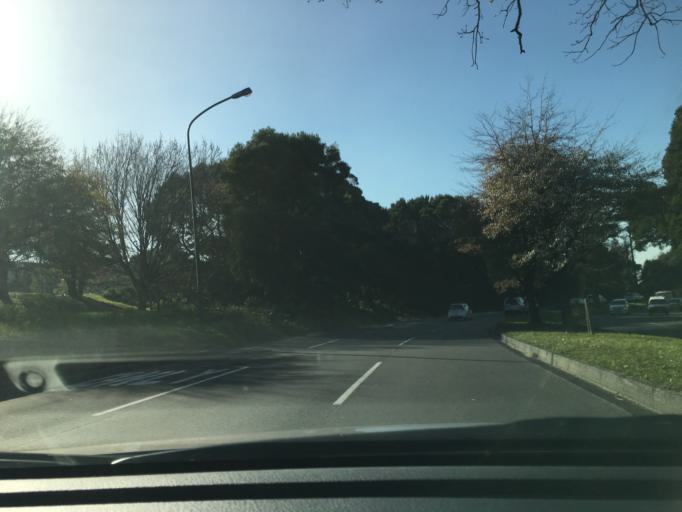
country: ZA
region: Western Cape
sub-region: City of Cape Town
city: Rosebank
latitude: -33.9617
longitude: 18.4603
